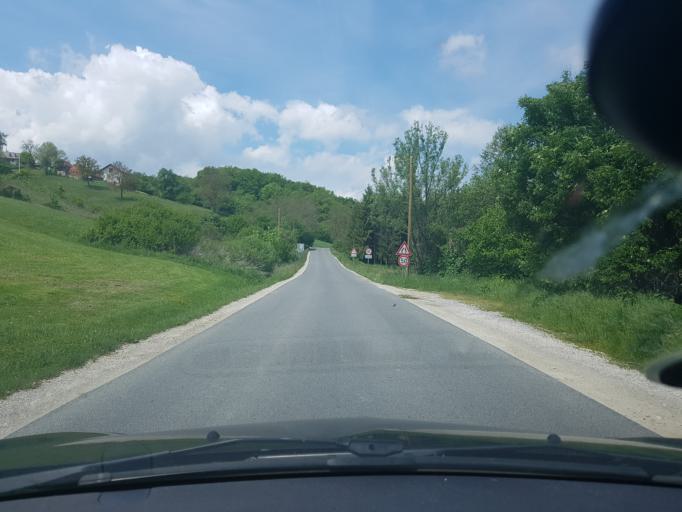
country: HR
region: Krapinsko-Zagorska
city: Pregrada
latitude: 46.1892
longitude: 15.7241
